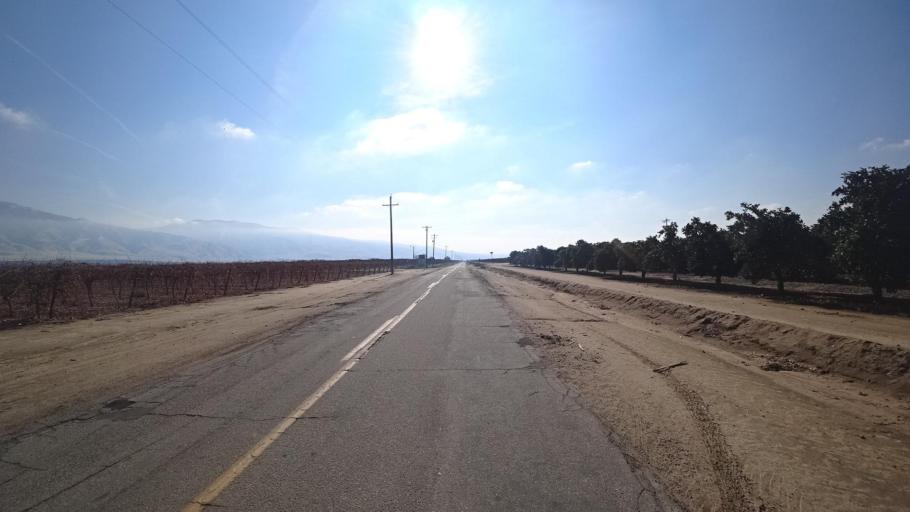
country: US
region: California
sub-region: Kern County
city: Arvin
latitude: 35.2540
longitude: -118.7886
